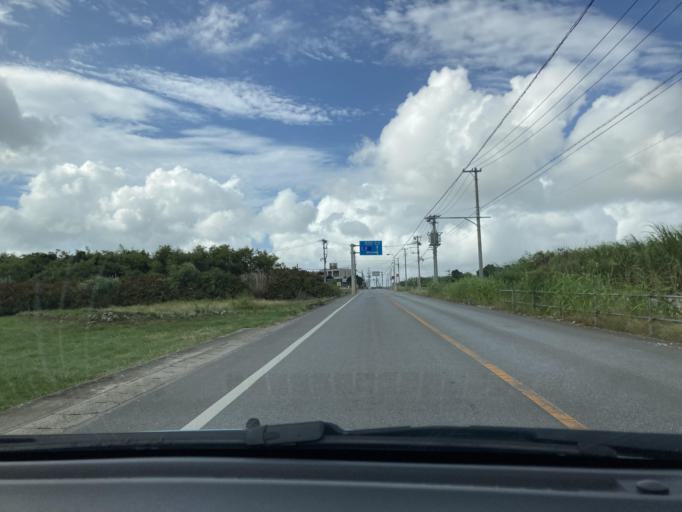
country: JP
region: Okinawa
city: Itoman
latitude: 26.1012
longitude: 127.6974
